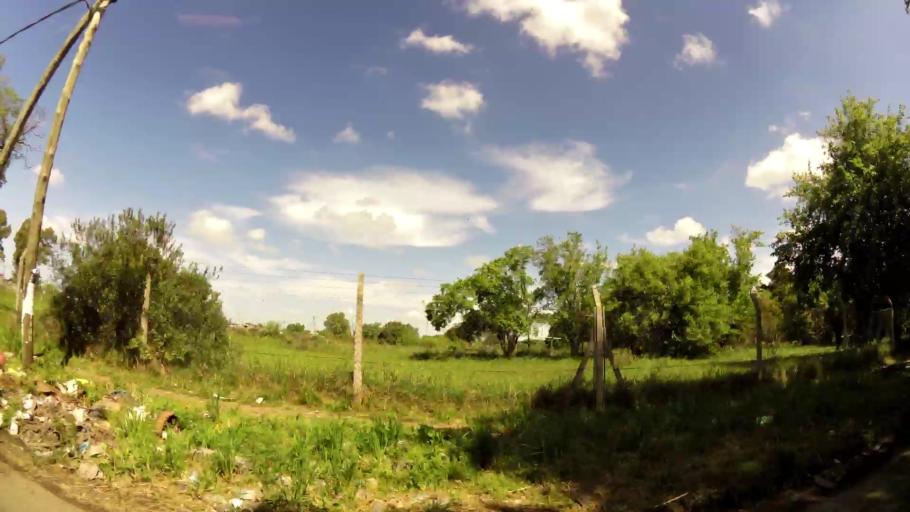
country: AR
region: Buenos Aires
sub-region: Partido de Quilmes
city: Quilmes
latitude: -34.8190
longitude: -58.2623
